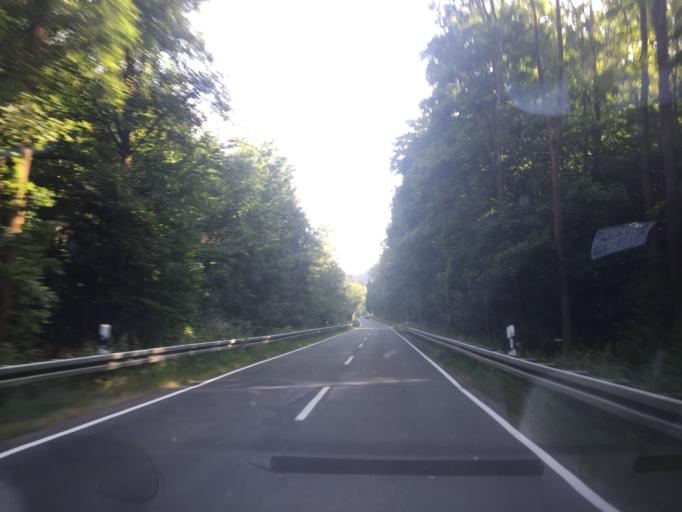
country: DE
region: Saxony-Anhalt
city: Darlingerode
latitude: 51.8143
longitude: 10.7366
